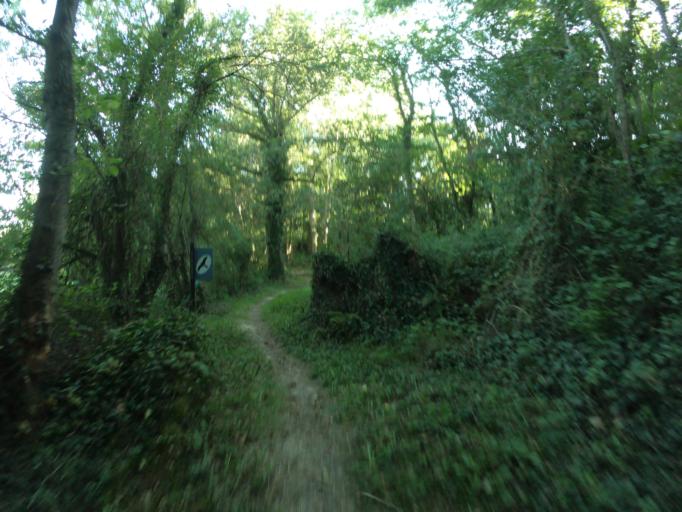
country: FR
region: Midi-Pyrenees
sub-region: Departement de l'Ariege
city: La Tour-du-Crieu
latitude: 43.0991
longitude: 1.7136
